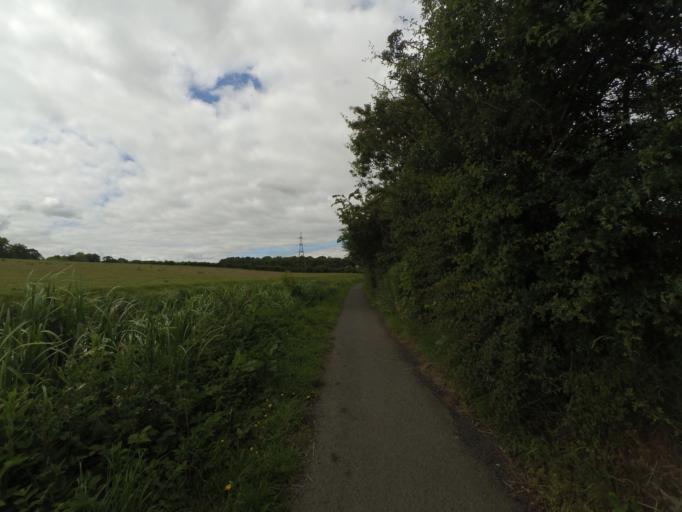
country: GB
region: Scotland
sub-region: Falkirk
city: Polmont
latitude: 55.9814
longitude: -3.6937
